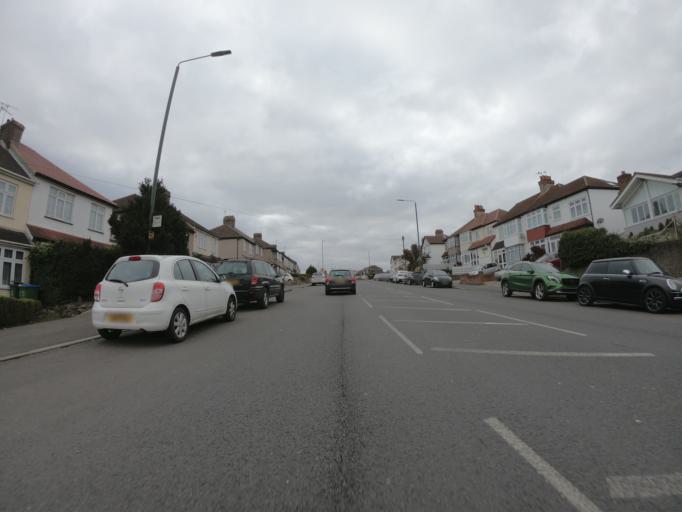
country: GB
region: England
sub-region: Greater London
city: Belvedere
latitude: 51.4789
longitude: 0.1418
